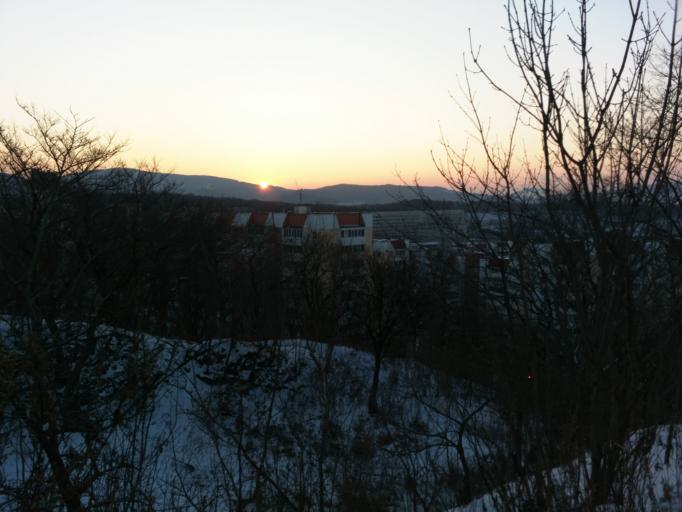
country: RU
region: Primorskiy
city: Vladivostok
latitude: 43.1793
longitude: 131.9289
